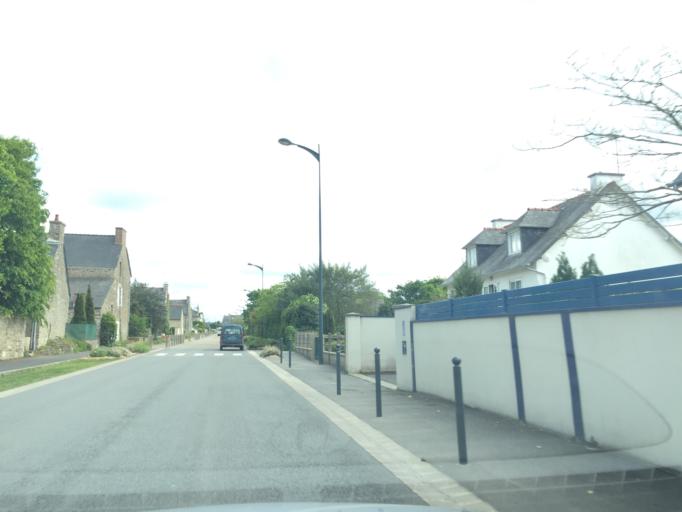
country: FR
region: Brittany
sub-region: Departement des Cotes-d'Armor
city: Lancieux
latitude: 48.6034
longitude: -2.1508
